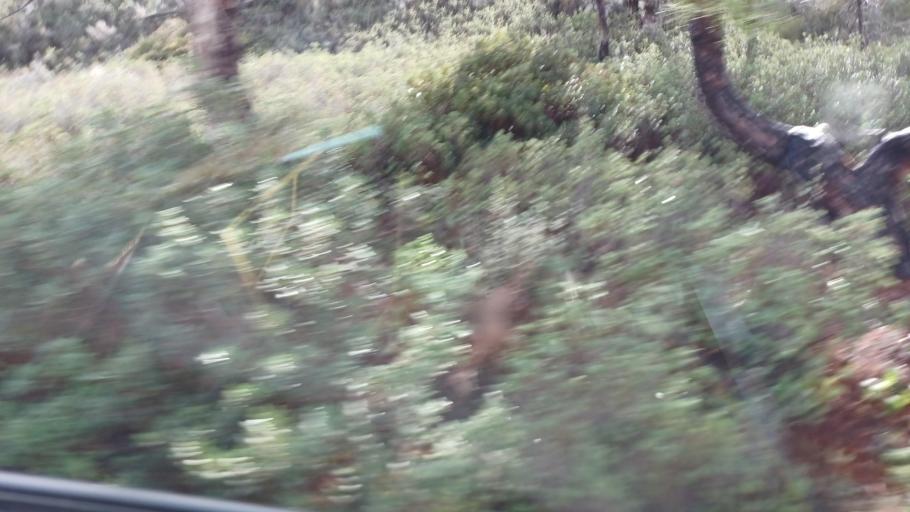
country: CY
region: Limassol
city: Sotira
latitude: 34.7056
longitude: 32.8664
